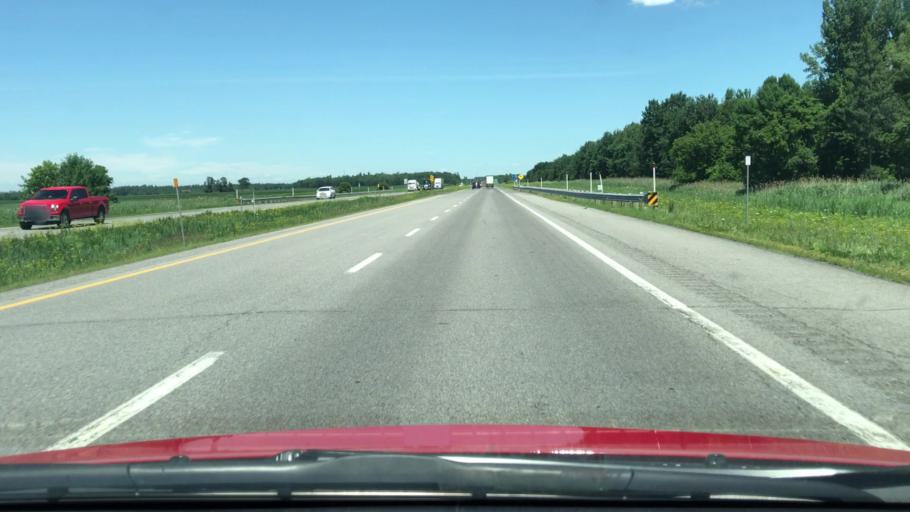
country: CA
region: Quebec
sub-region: Monteregie
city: Napierville
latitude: 45.1721
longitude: -73.4626
